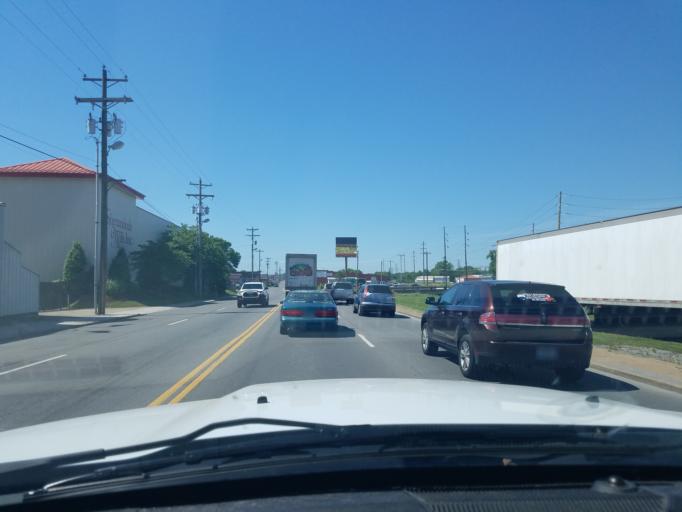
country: US
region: Tennessee
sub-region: Wilson County
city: Lebanon
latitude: 36.2060
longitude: -86.2914
